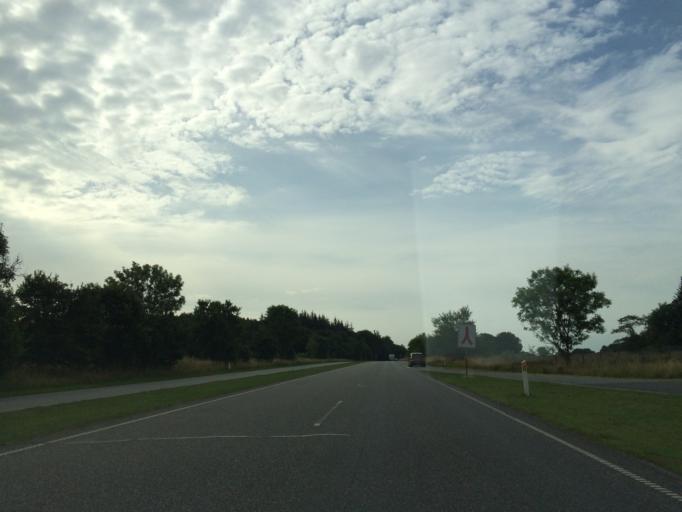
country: DK
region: South Denmark
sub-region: Kolding Kommune
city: Kolding
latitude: 55.5206
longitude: 9.4995
